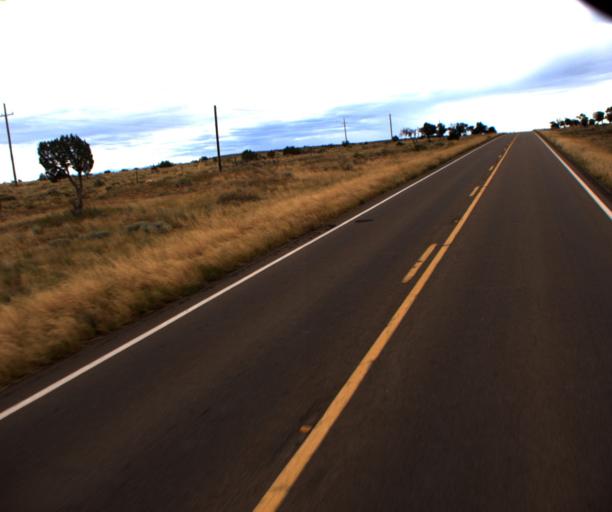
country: US
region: Arizona
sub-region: Navajo County
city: Snowflake
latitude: 34.5542
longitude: -110.0807
